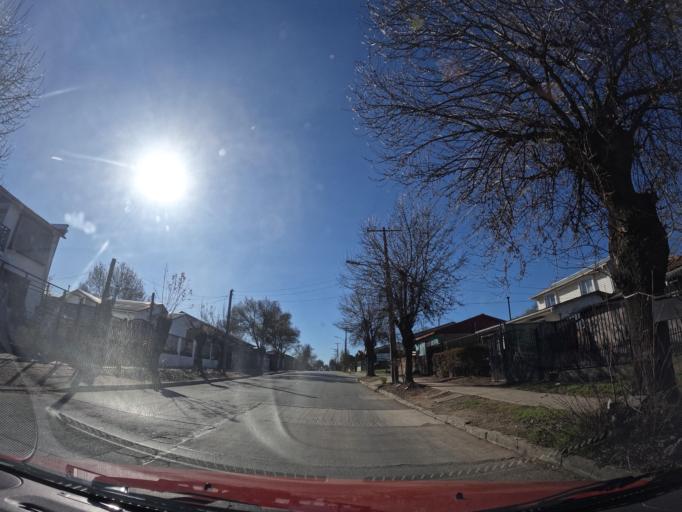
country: CL
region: Maule
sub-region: Provincia de Cauquenes
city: Cauquenes
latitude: -35.9854
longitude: -72.3185
